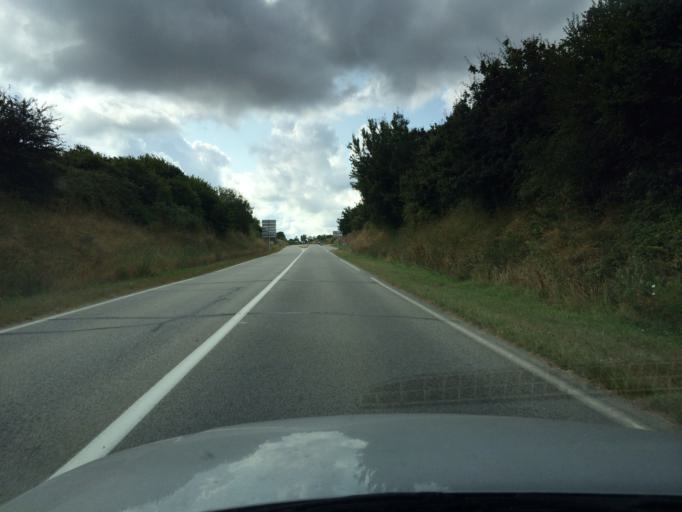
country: FR
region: Lower Normandy
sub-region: Departement de la Manche
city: Martinvast
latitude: 49.5781
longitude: -1.7065
